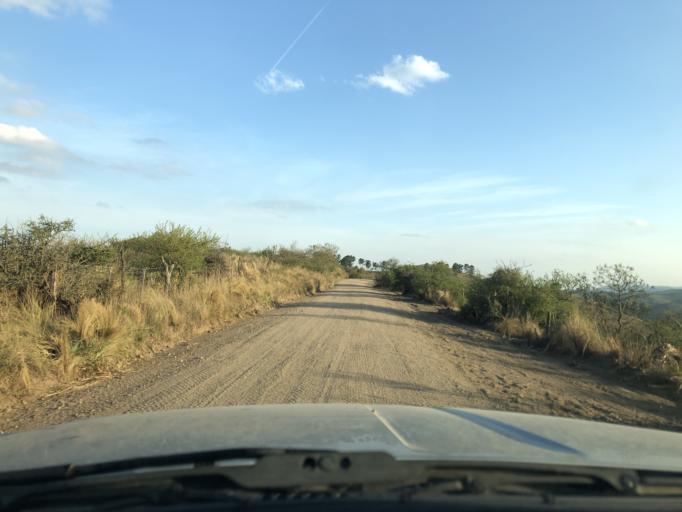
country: AR
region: Cordoba
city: Agua de Oro
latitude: -31.0582
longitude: -64.3502
